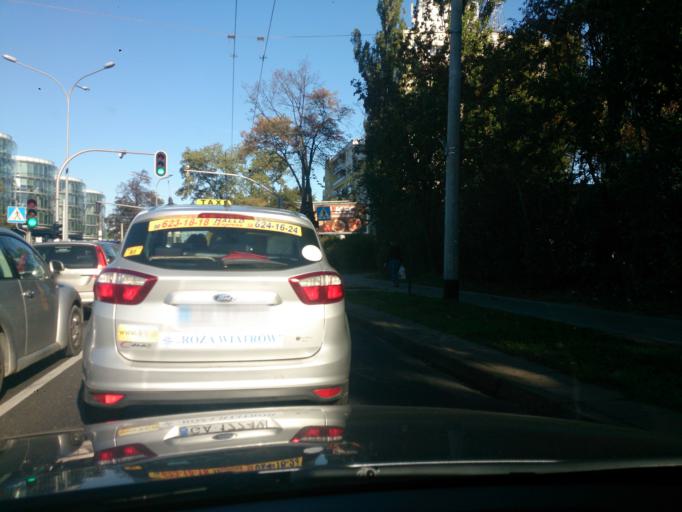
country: PL
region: Pomeranian Voivodeship
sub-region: Gdynia
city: Gdynia
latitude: 54.4920
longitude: 18.5411
